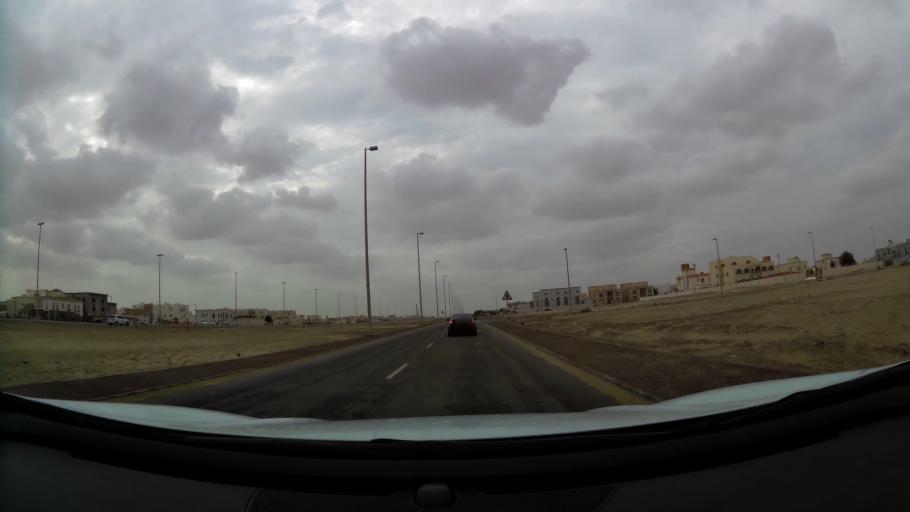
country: AE
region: Abu Dhabi
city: Abu Dhabi
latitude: 24.3469
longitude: 54.6281
